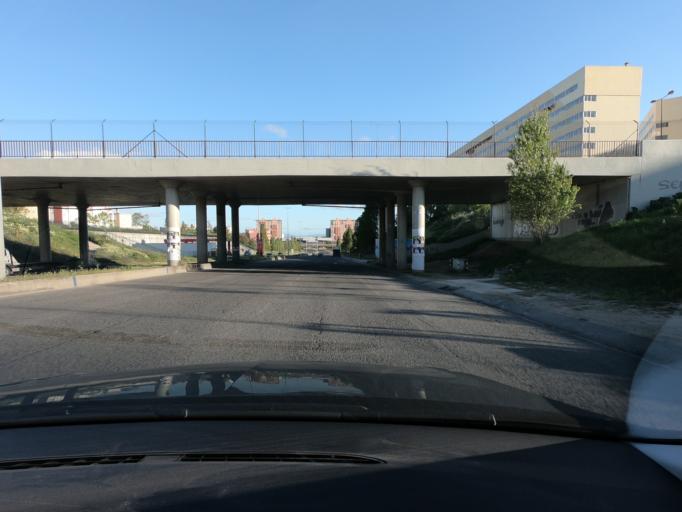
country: PT
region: Lisbon
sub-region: Loures
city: Moscavide
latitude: 38.7562
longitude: -9.1195
